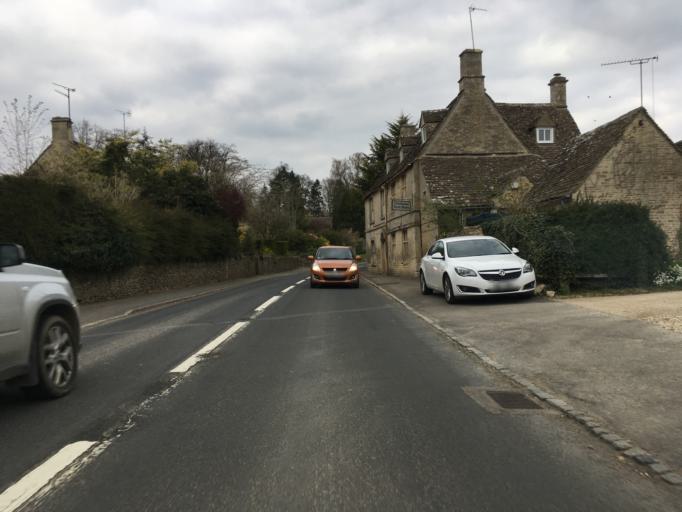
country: GB
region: England
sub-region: Gloucestershire
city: Cirencester
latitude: 51.7455
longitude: -1.8899
